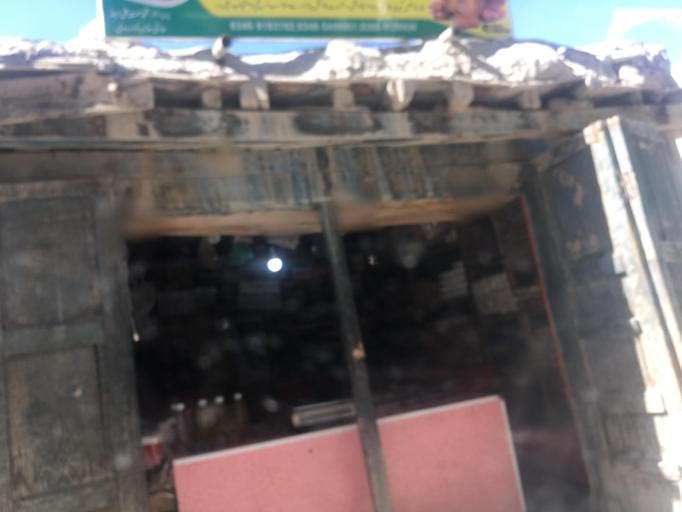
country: PK
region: Gilgit-Baltistan
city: Skardu
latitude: 35.2989
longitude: 75.6327
